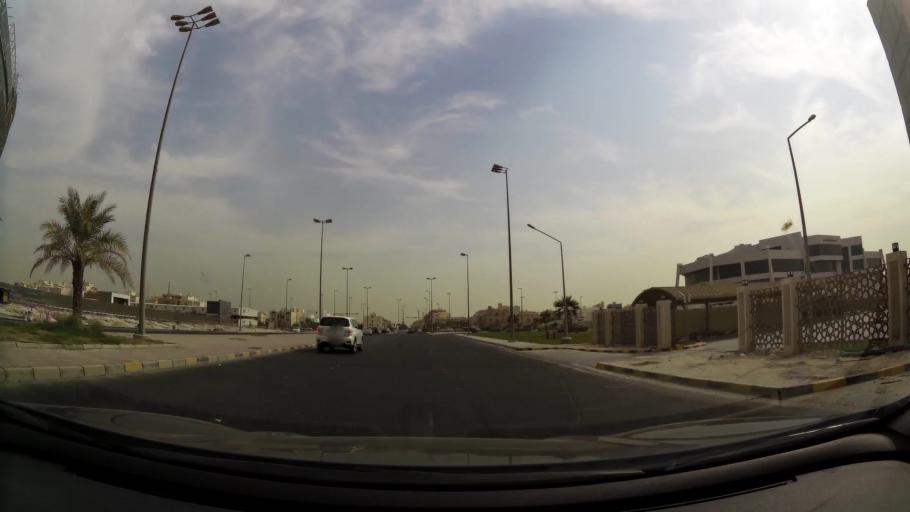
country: KW
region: Mubarak al Kabir
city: Sabah as Salim
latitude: 29.2713
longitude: 48.0203
